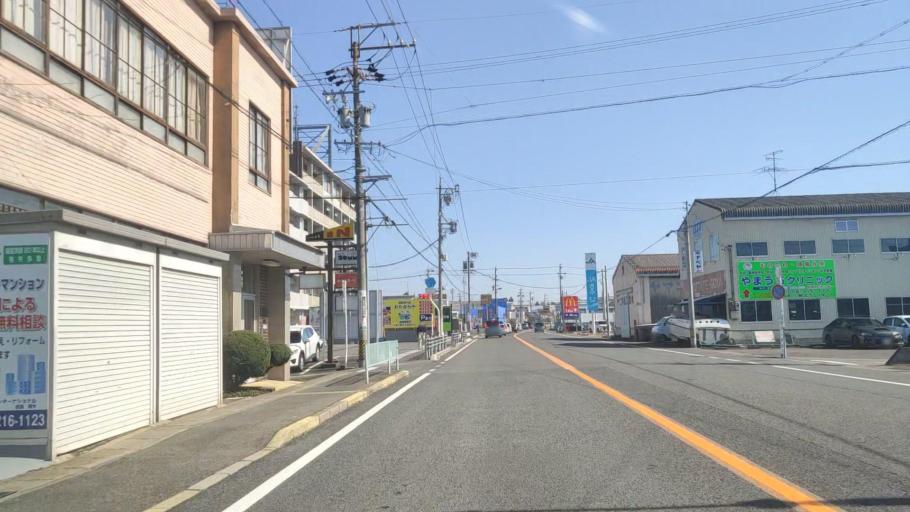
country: JP
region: Gifu
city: Gifu-shi
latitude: 35.3973
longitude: 136.7668
